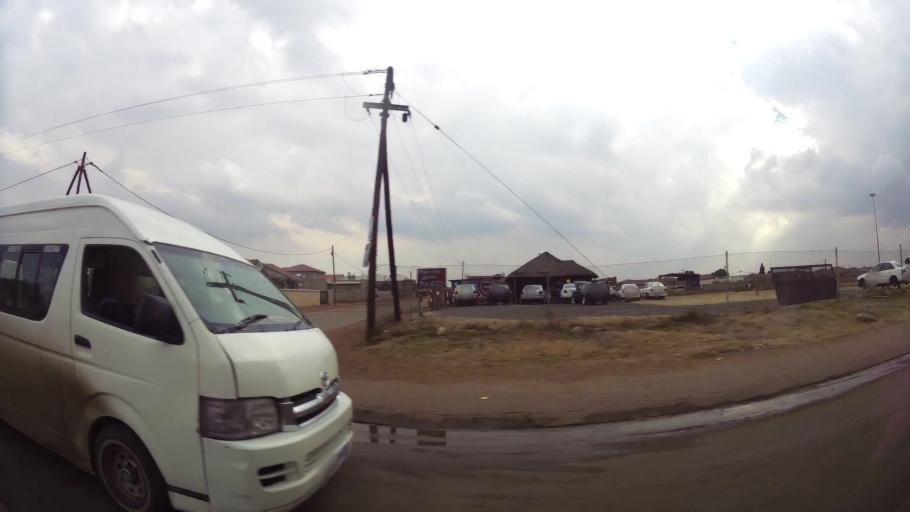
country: ZA
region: Gauteng
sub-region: Ekurhuleni Metropolitan Municipality
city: Germiston
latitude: -26.3828
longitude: 28.1621
